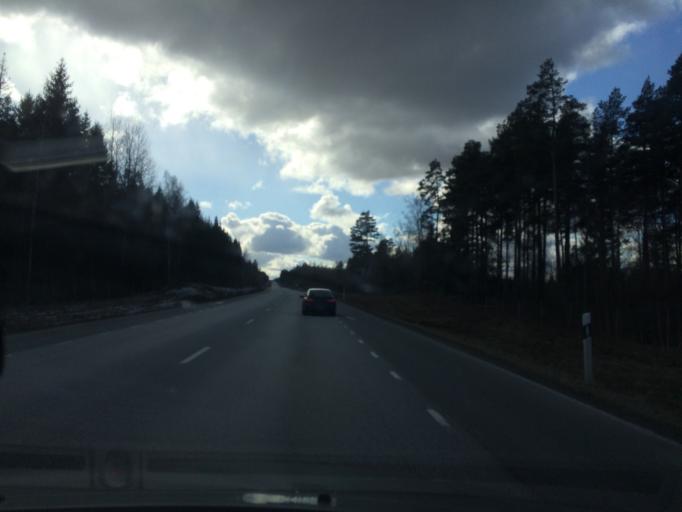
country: SE
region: Vaestra Goetaland
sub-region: Mariestads Kommun
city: Mariestad
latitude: 58.6242
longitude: 13.6689
